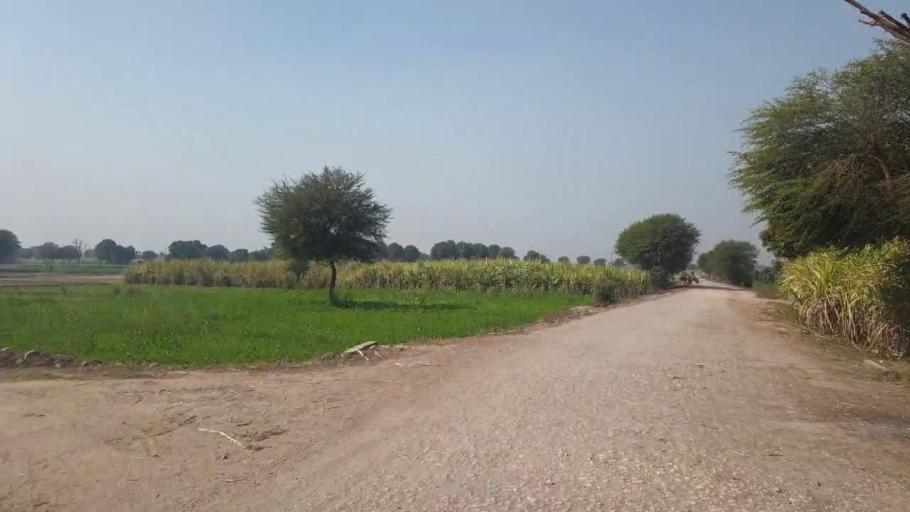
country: PK
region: Sindh
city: Tando Jam
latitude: 25.3278
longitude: 68.6142
